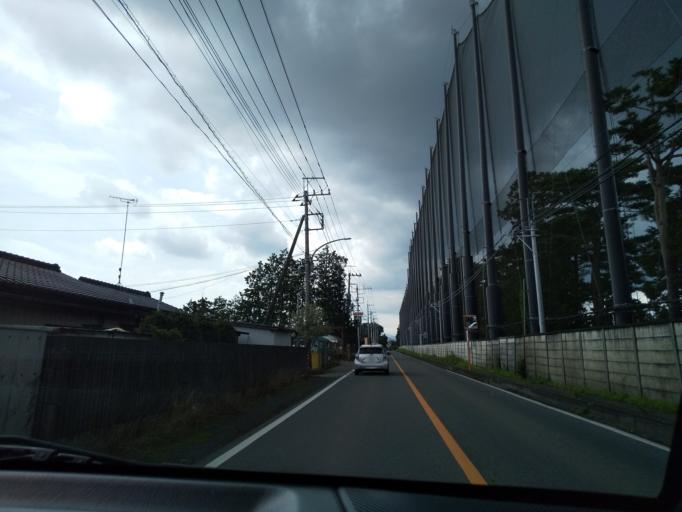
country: JP
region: Saitama
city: Hanno
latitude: 35.8595
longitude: 139.3535
